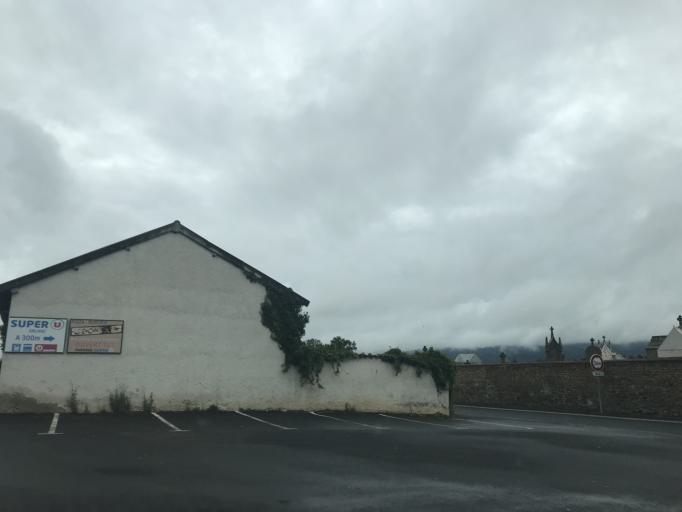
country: FR
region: Auvergne
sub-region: Departement du Puy-de-Dome
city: Arlanc
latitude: 45.4168
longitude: 3.7269
